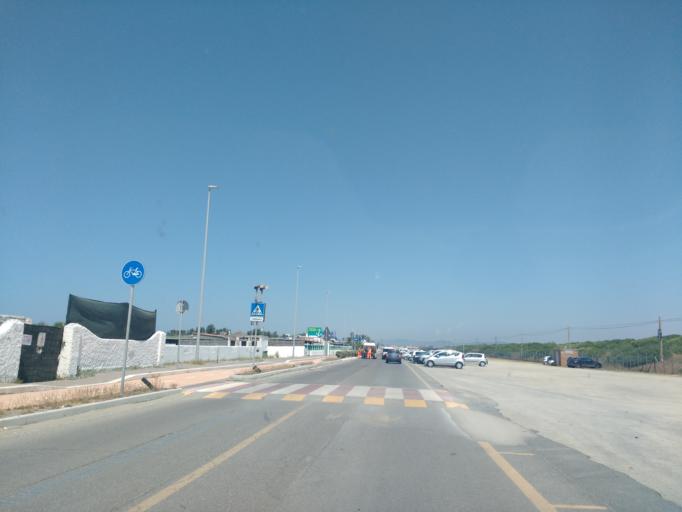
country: IT
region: Latium
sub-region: Citta metropolitana di Roma Capitale
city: Passo Oscuro
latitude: 41.8805
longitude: 12.1744
